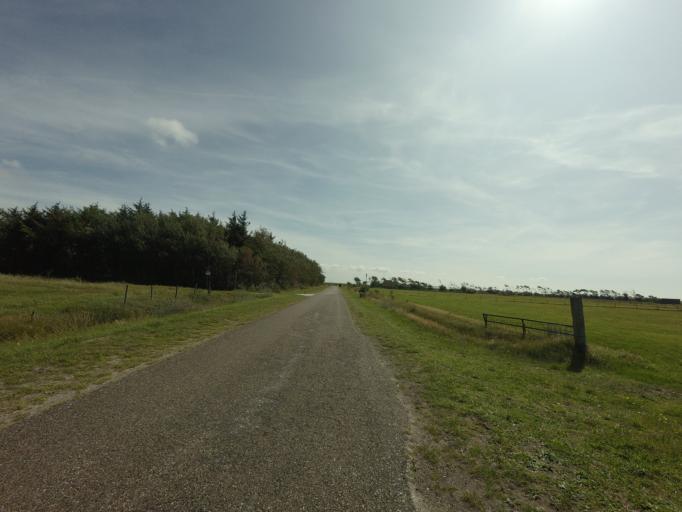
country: NL
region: Friesland
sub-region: Gemeente Ameland
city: Hollum
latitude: 53.4434
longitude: 5.6627
